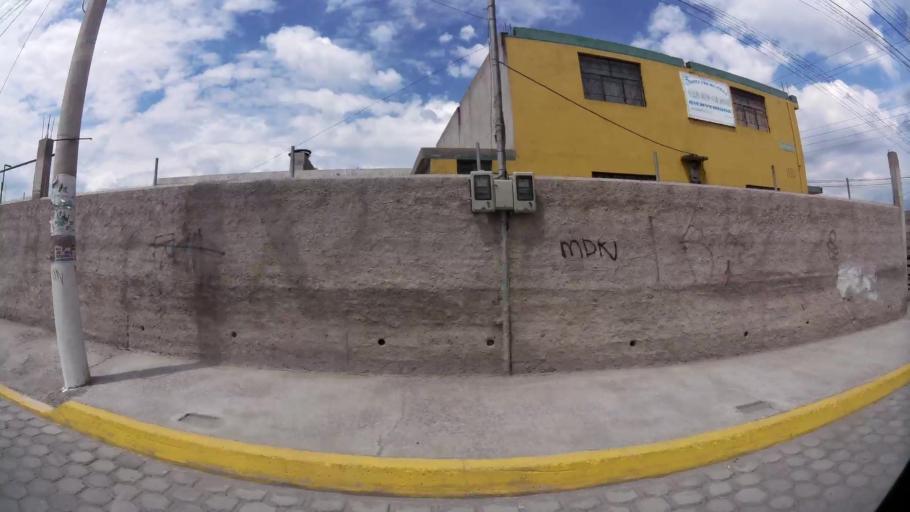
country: EC
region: Pichincha
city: Quito
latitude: -0.0710
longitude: -78.4152
